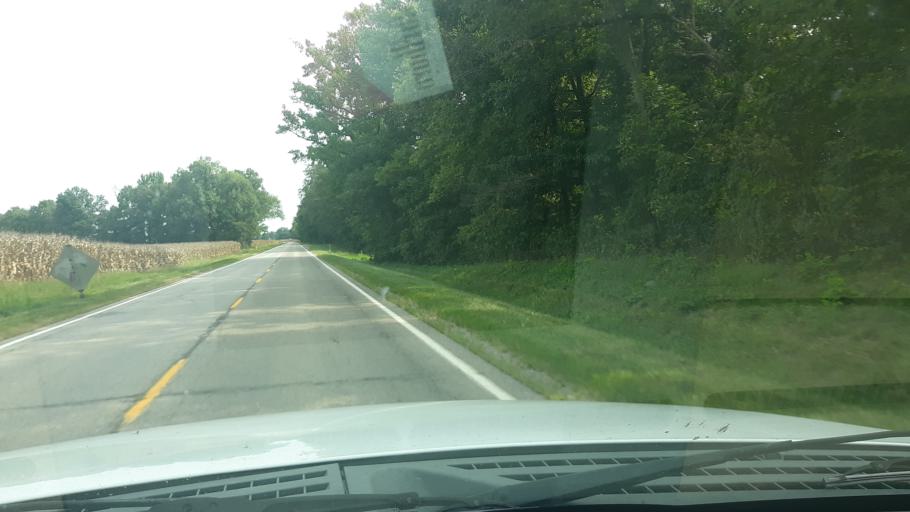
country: US
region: Illinois
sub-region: Edwards County
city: Grayville
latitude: 38.3003
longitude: -87.9519
